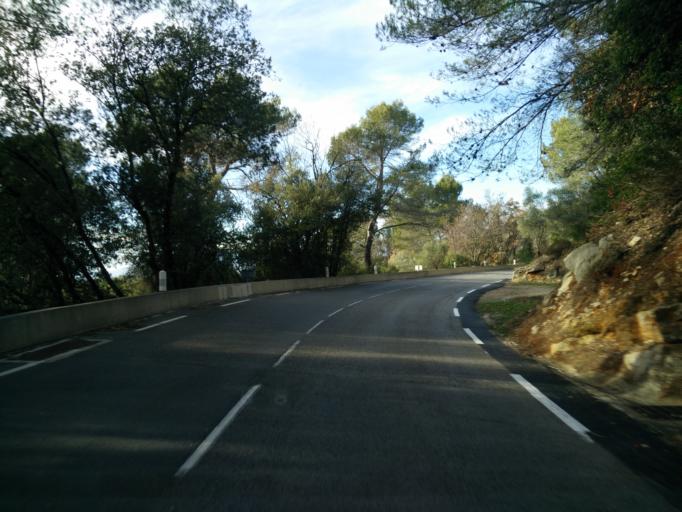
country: FR
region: Provence-Alpes-Cote d'Azur
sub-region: Departement des Alpes-Maritimes
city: Le Tignet
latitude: 43.6358
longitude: 6.8288
